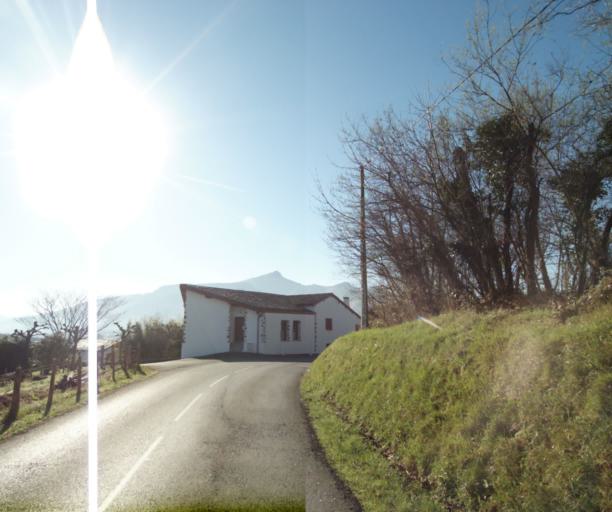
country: FR
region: Aquitaine
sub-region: Departement des Pyrenees-Atlantiques
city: Ciboure
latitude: 43.3503
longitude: -1.6681
